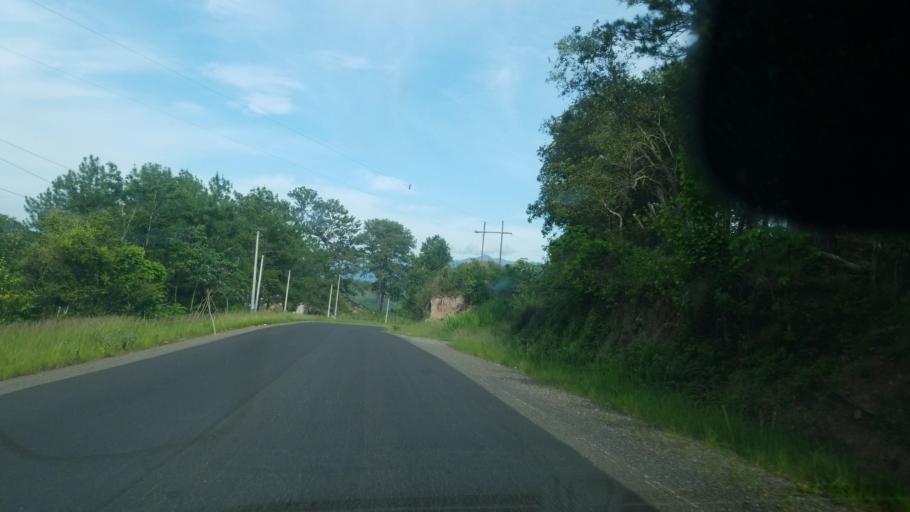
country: HN
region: Santa Barbara
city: Trinidad
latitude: 15.1726
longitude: -88.2658
